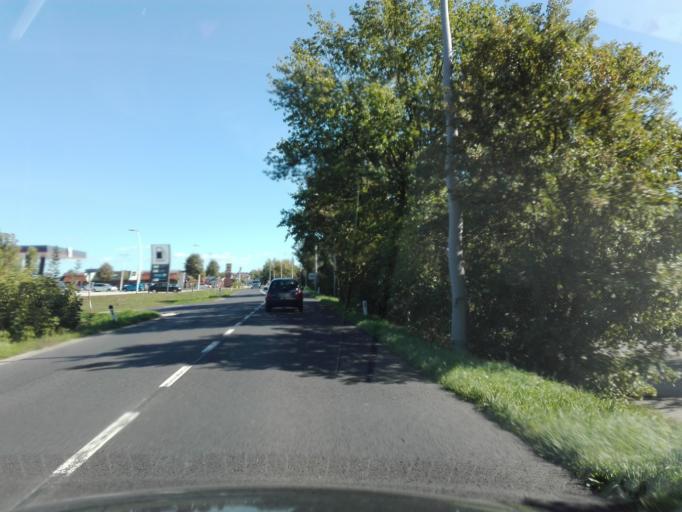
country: AT
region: Upper Austria
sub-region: Politischer Bezirk Linz-Land
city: Enns
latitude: 48.2160
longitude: 14.4571
